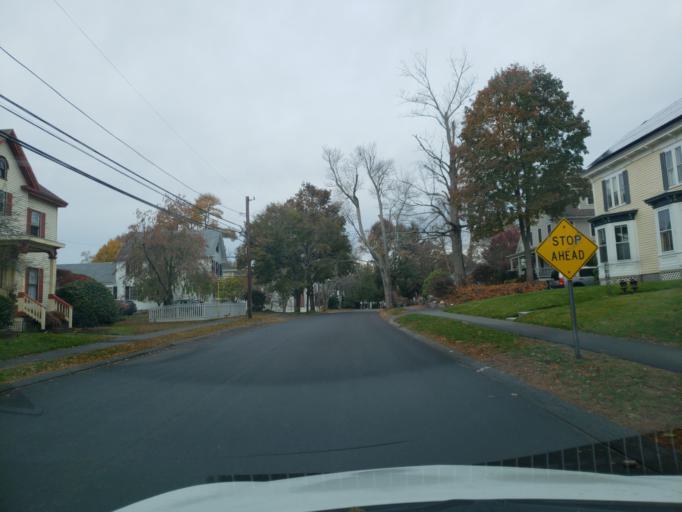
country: US
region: Massachusetts
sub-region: Essex County
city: Andover
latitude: 42.6587
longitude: -71.1352
